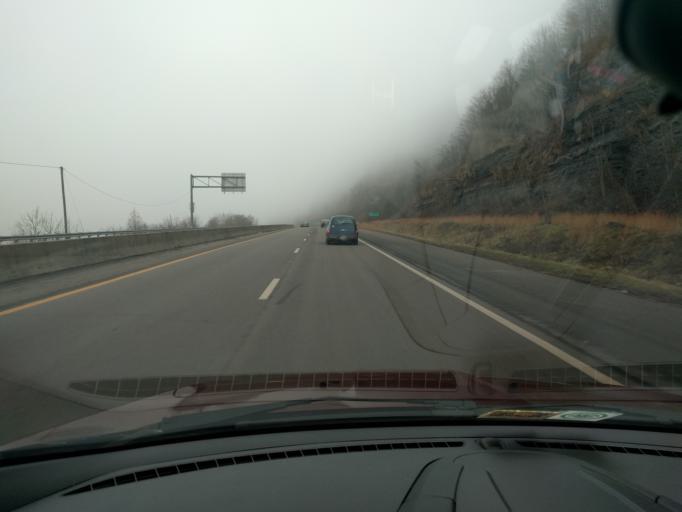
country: US
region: West Virginia
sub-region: Kanawha County
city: Chesapeake
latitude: 38.2067
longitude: -81.5049
